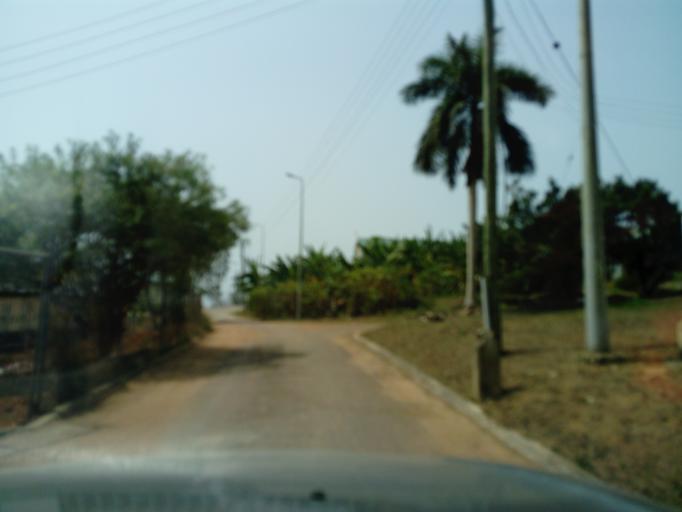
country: GH
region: Central
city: Cape Coast
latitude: 5.1051
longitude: -1.2734
